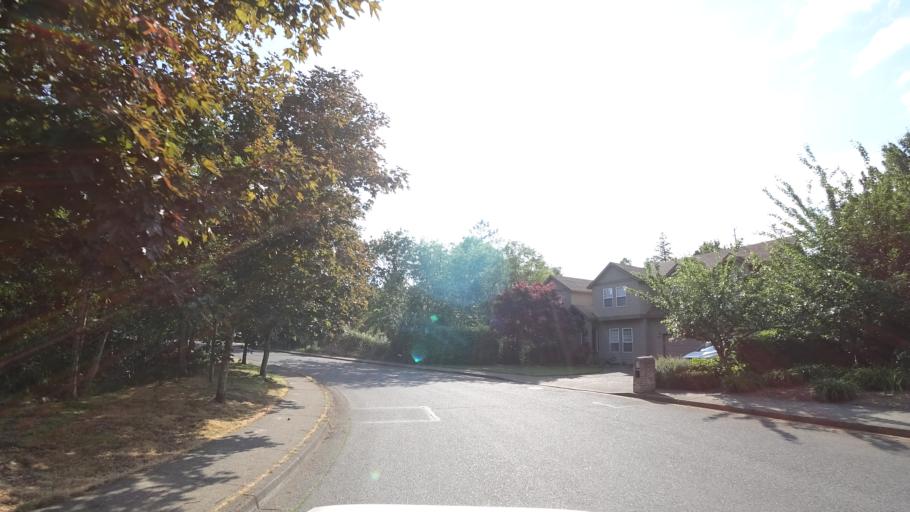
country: US
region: Oregon
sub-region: Washington County
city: Garden Home-Whitford
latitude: 45.4617
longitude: -122.7429
